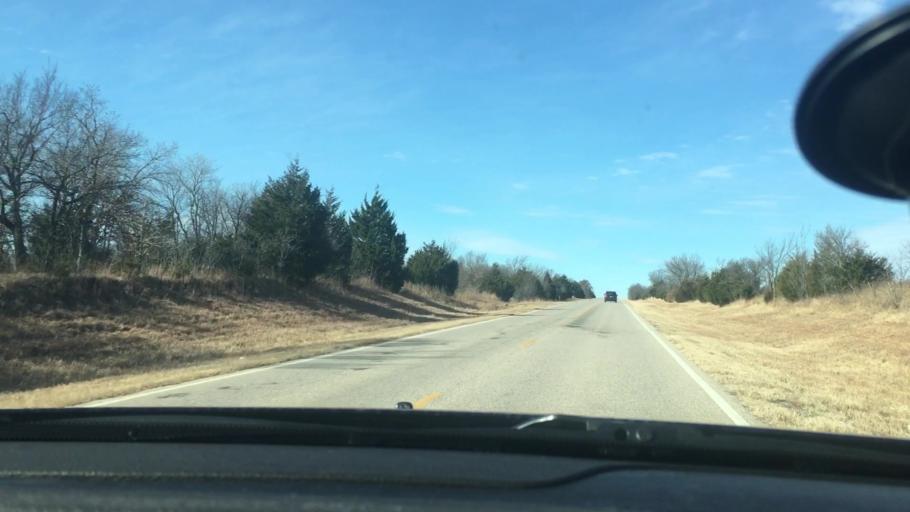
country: US
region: Oklahoma
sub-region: Garvin County
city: Stratford
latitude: 34.9859
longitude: -97.0094
